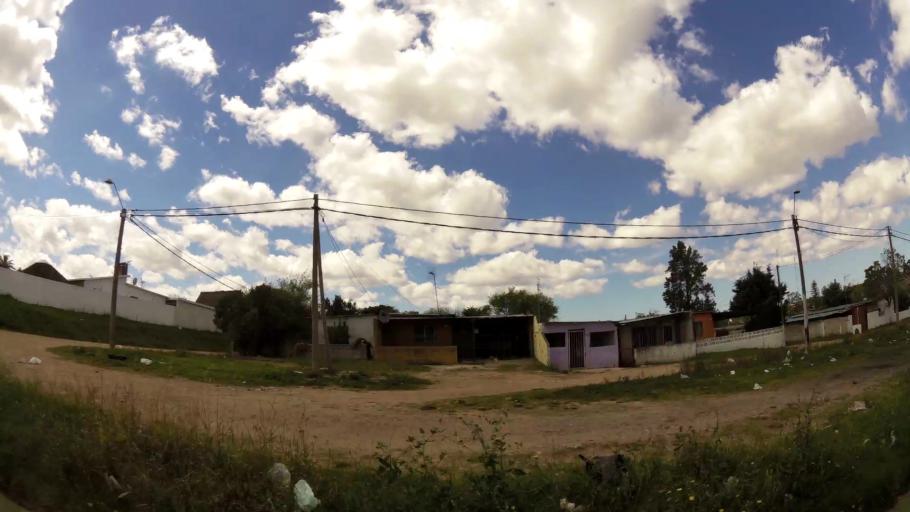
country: UY
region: Canelones
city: Paso de Carrasco
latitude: -34.8279
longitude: -56.1194
